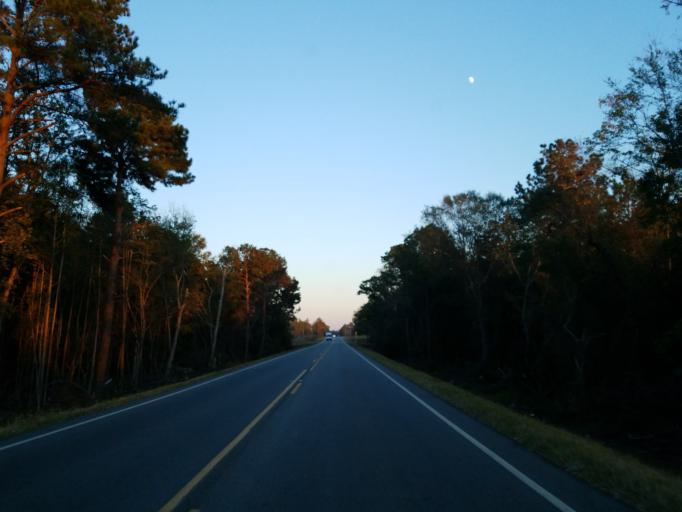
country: US
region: Georgia
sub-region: Irwin County
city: Ocilla
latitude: 31.6469
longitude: -83.3657
